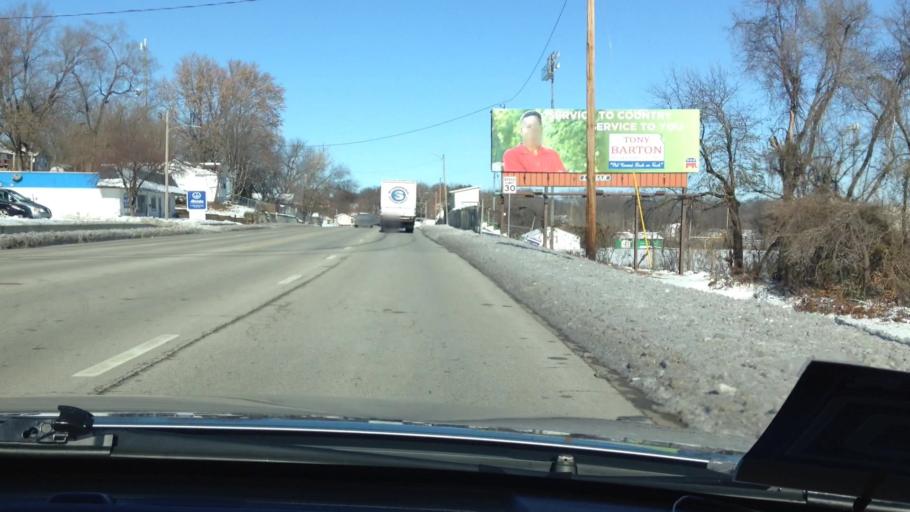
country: US
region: Kansas
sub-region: Leavenworth County
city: Leavenworth
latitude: 39.3003
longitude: -94.9088
